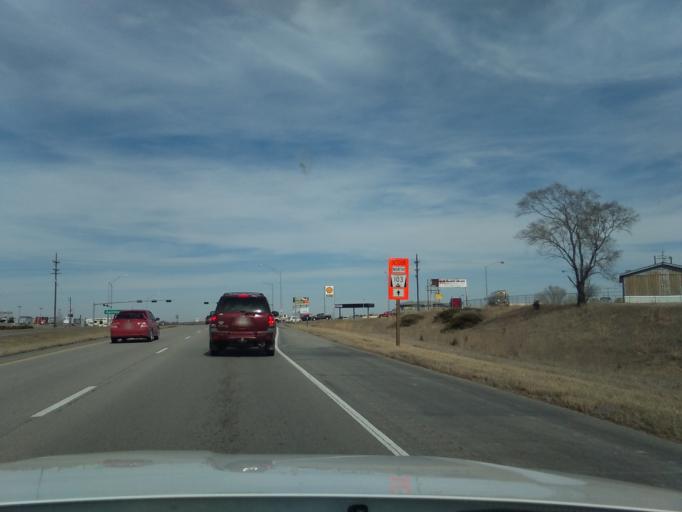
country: US
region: Nebraska
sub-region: Lancaster County
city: Hickman
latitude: 40.6958
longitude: -96.7050
